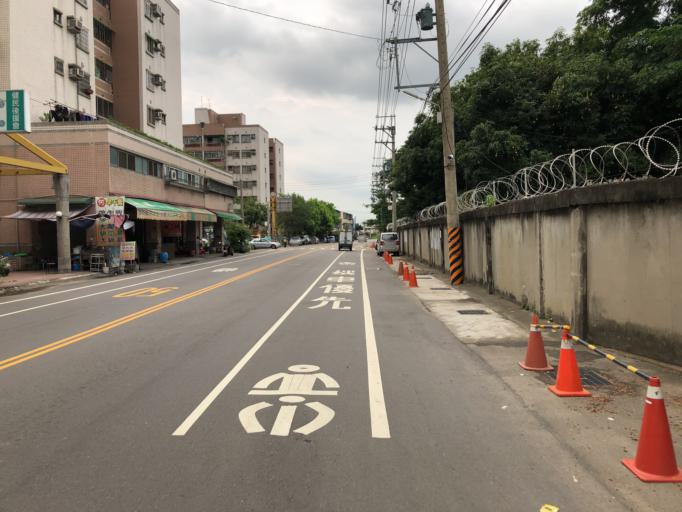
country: TW
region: Taiwan
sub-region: Taichung City
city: Taichung
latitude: 24.0926
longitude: 120.7296
